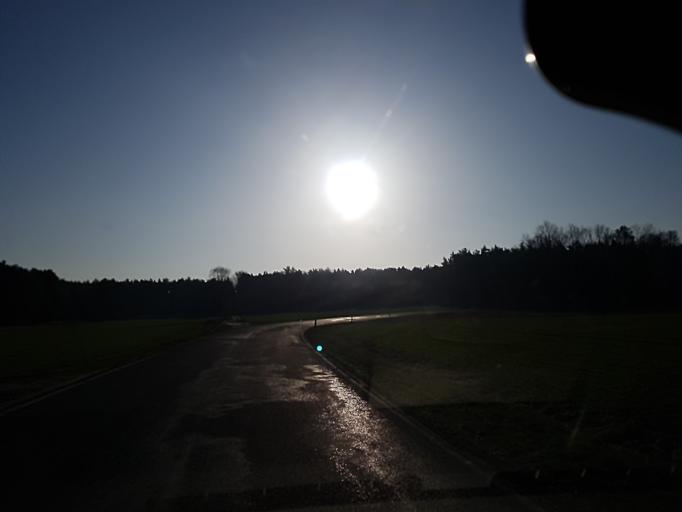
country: DE
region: Brandenburg
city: Schonborn
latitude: 51.5544
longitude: 13.4913
